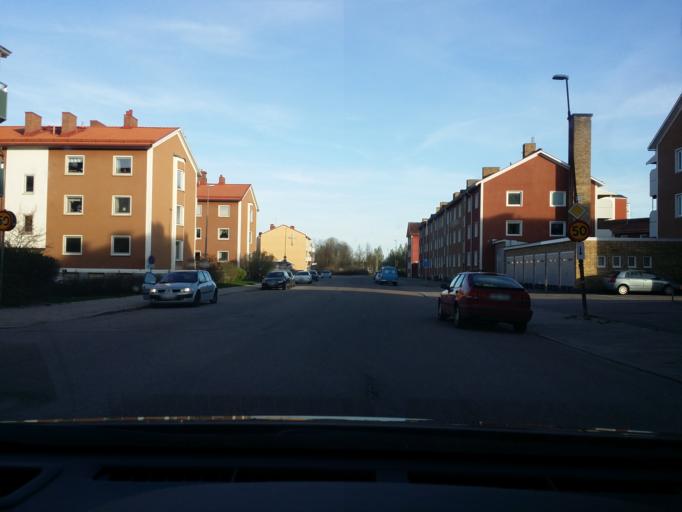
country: SE
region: Dalarna
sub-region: Avesta Kommun
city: Avesta
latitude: 60.1423
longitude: 16.1668
